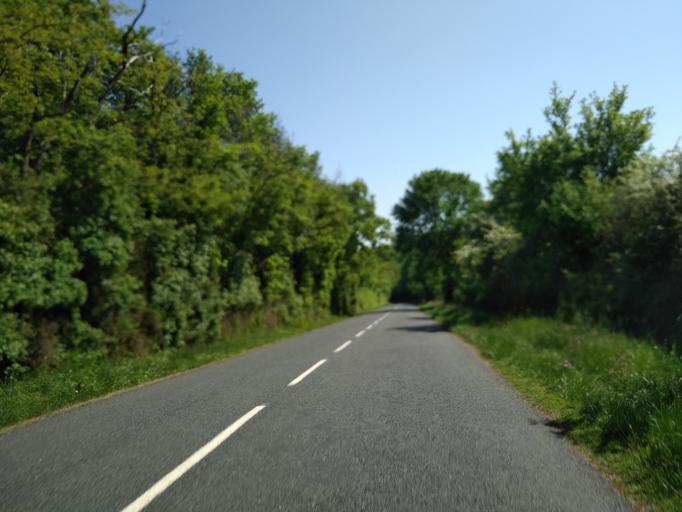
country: FR
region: Rhone-Alpes
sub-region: Departement du Rhone
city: Limonest
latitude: 45.8347
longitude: 4.7994
